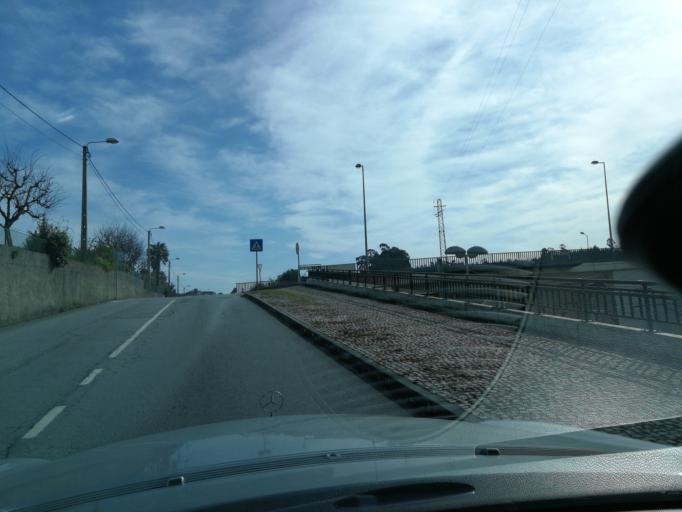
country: PT
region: Braga
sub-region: Vila Nova de Famalicao
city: Vila Nova de Famalicao
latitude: 41.4299
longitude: -8.5222
